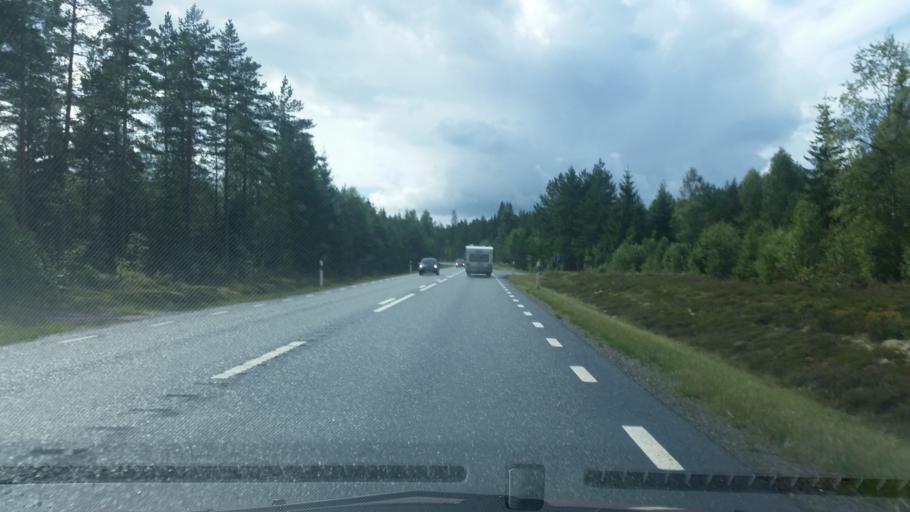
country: SE
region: Joenkoeping
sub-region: Gislaveds Kommun
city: Gislaved
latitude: 57.3825
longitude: 13.5816
